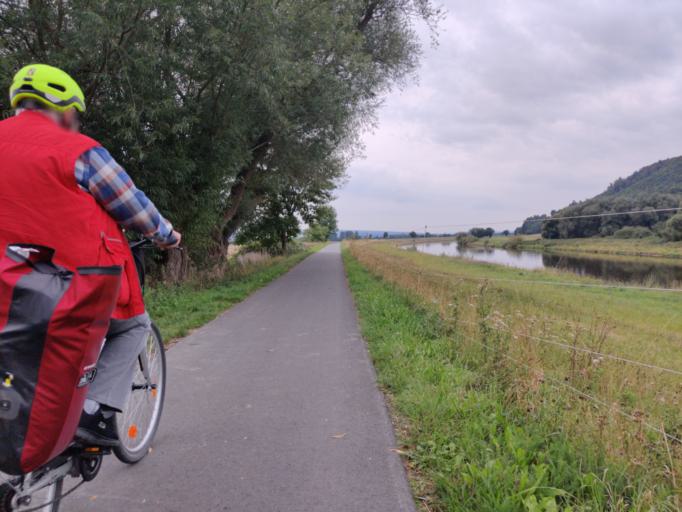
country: DE
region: Lower Saxony
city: Bevern
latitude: 51.8760
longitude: 9.4685
